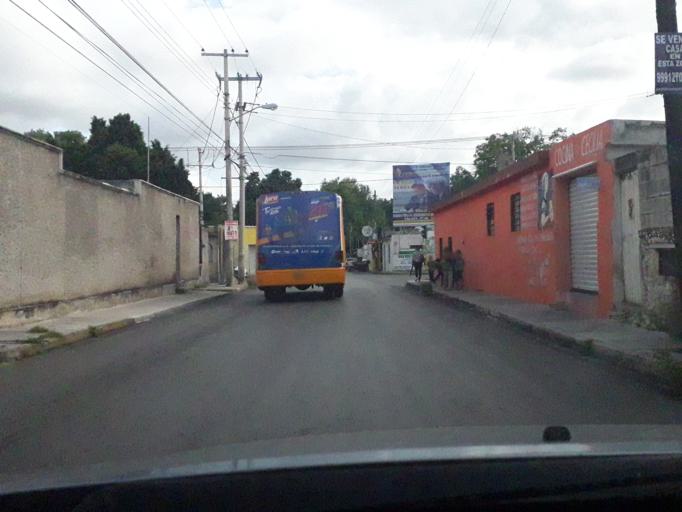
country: MX
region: Yucatan
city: Merida
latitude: 21.0161
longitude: -89.6319
